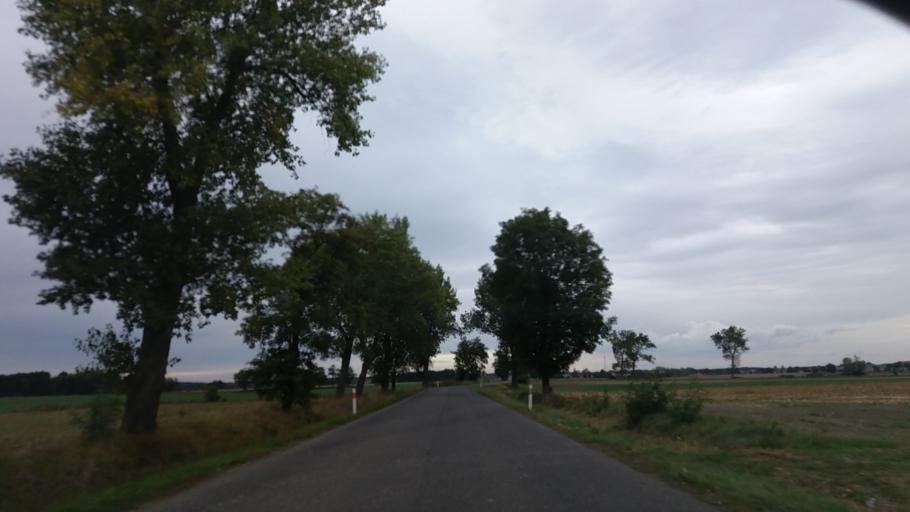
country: PL
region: Lower Silesian Voivodeship
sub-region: Powiat legnicki
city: Prochowice
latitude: 51.2013
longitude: 16.3464
